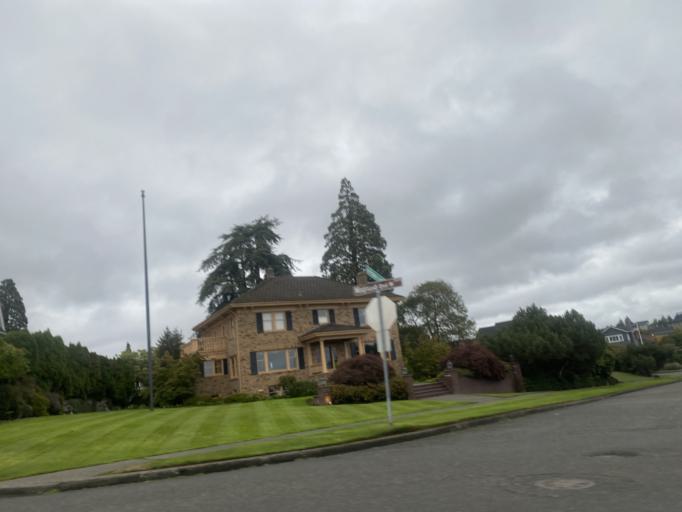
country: US
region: Washington
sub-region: King County
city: Seattle
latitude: 47.6360
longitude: -122.4052
